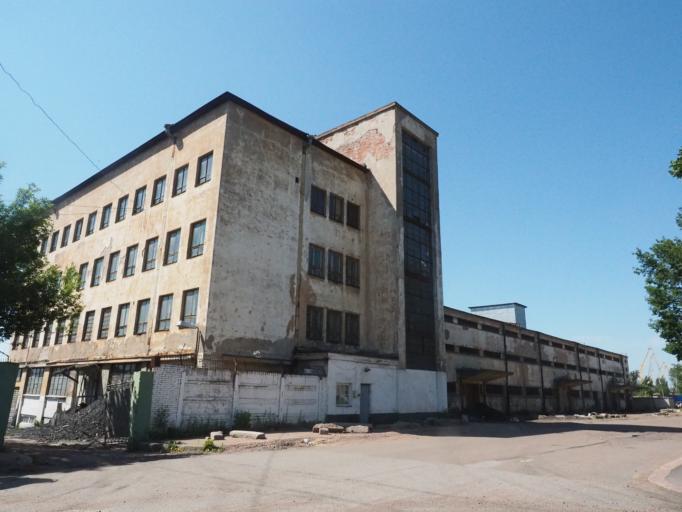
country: RU
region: Leningrad
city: Vyborg
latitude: 60.7043
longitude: 28.7409
